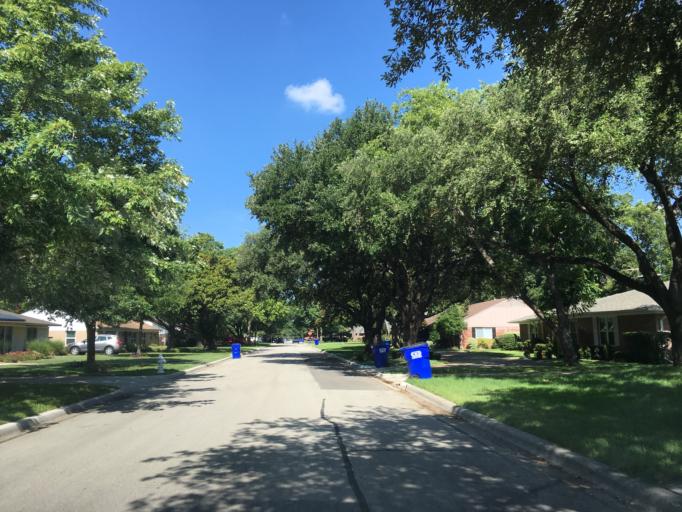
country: US
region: Texas
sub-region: Dallas County
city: Farmers Branch
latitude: 32.9210
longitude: -96.8751
